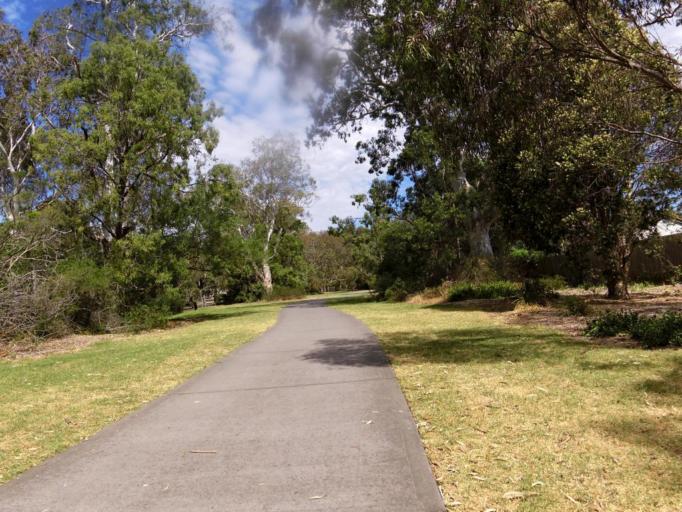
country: AU
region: Victoria
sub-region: Glen Eira
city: Murrumbeena
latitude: -37.8922
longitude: 145.0749
